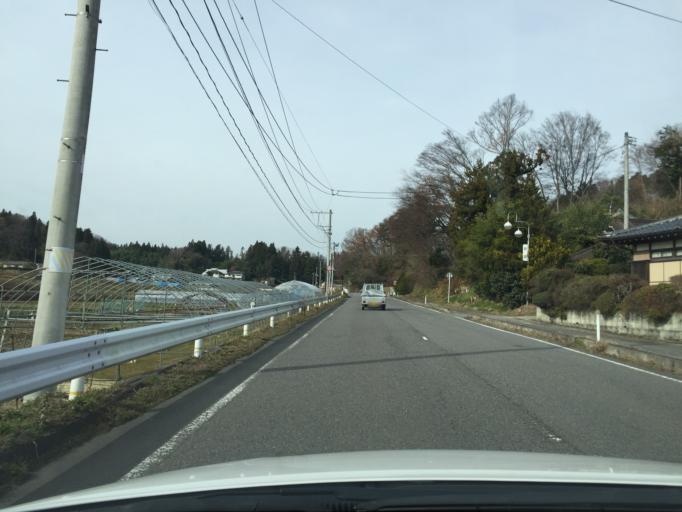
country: JP
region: Fukushima
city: Funehikimachi-funehiki
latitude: 37.4063
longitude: 140.5914
